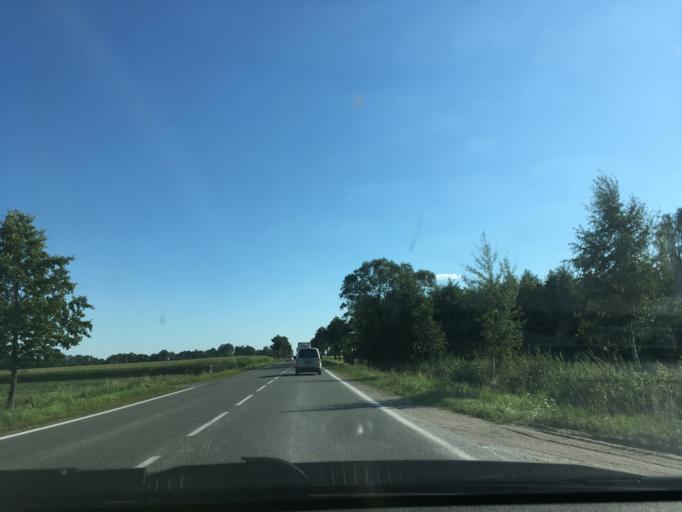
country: PL
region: Podlasie
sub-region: Powiat sokolski
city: Janow
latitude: 53.4027
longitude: 23.1163
